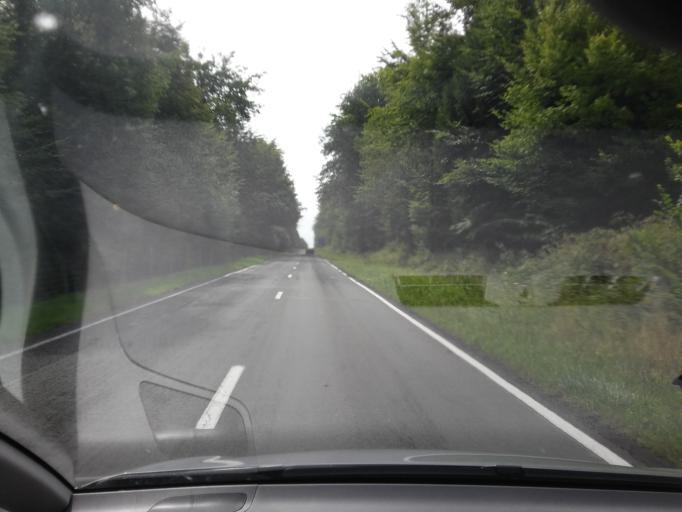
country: BE
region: Wallonia
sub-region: Province du Luxembourg
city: Chiny
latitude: 49.7657
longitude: 5.3636
